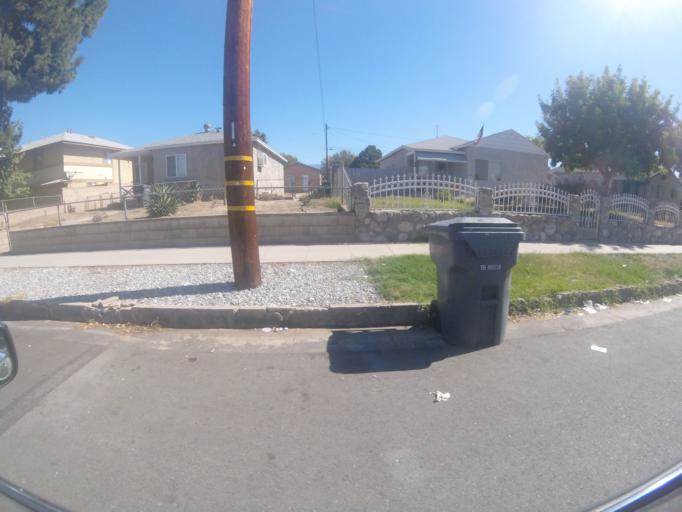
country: US
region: California
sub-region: San Bernardino County
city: Redlands
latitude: 34.0640
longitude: -117.1771
